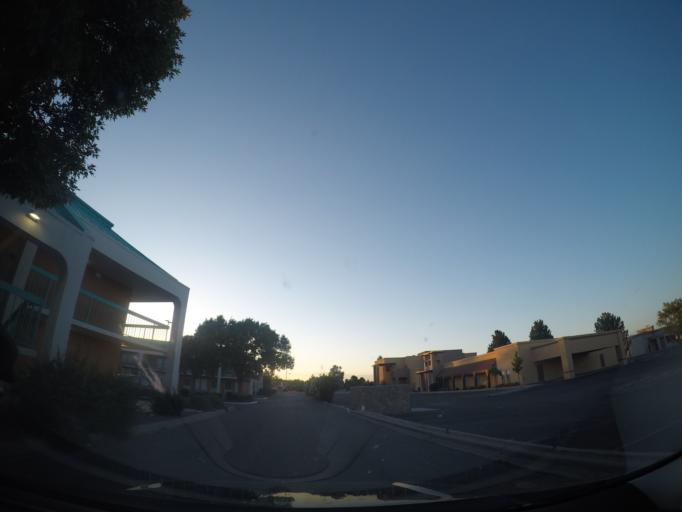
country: US
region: New Mexico
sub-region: Dona Ana County
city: Las Cruces
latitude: 32.2921
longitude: -106.7862
